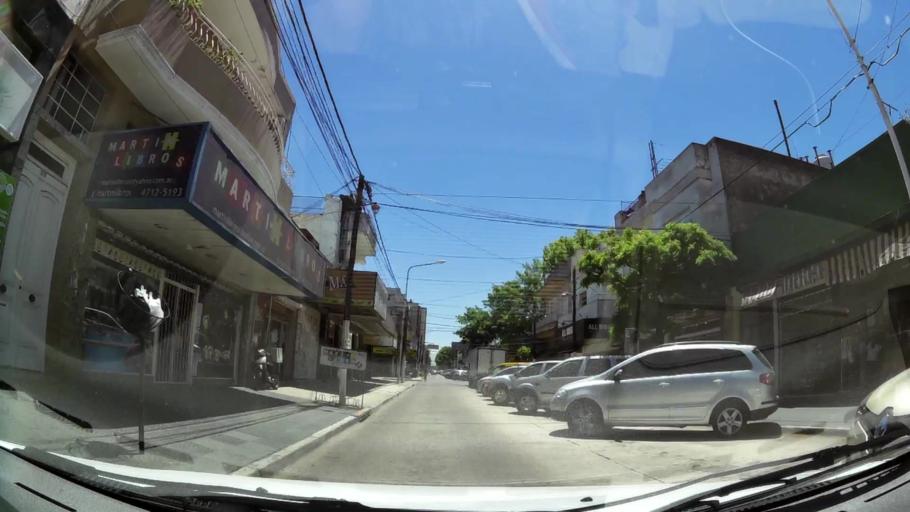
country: AR
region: Buenos Aires
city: Caseros
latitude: -34.6009
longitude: -58.5440
